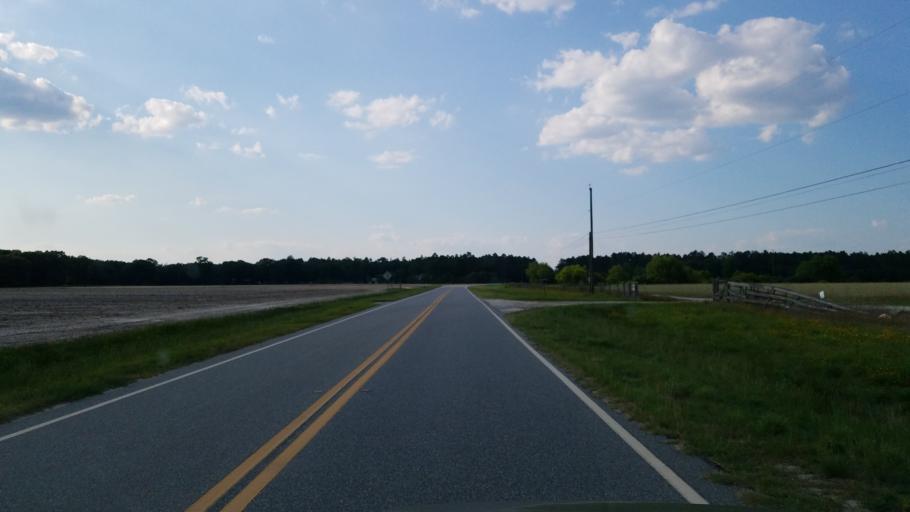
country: US
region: Georgia
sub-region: Echols County
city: Statenville
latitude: 30.7481
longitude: -83.0548
